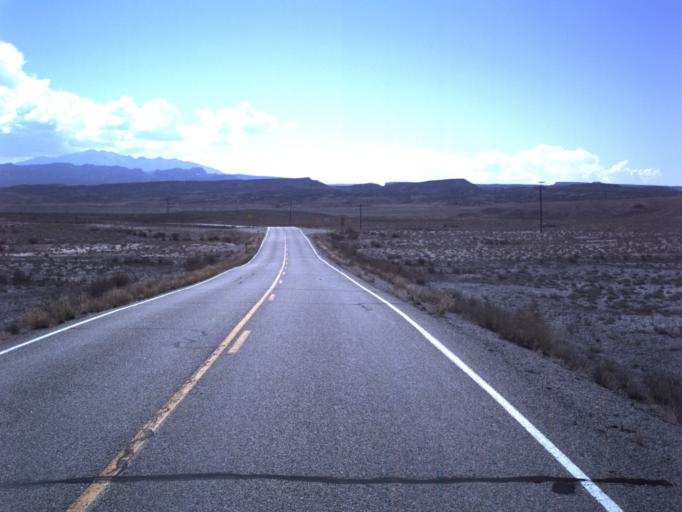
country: US
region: Utah
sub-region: Grand County
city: Moab
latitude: 38.8856
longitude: -109.3121
